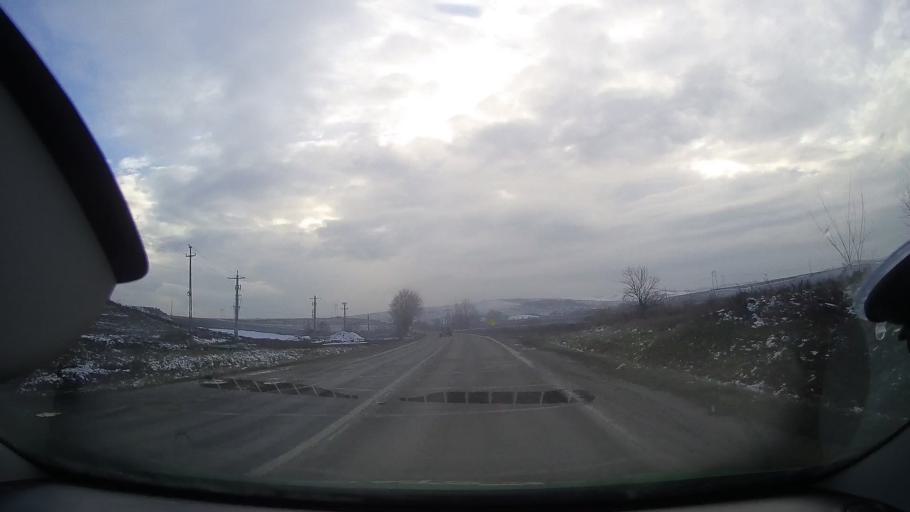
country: RO
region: Mures
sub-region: Comuna Iernut
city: Iernut
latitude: 46.4277
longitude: 24.2603
